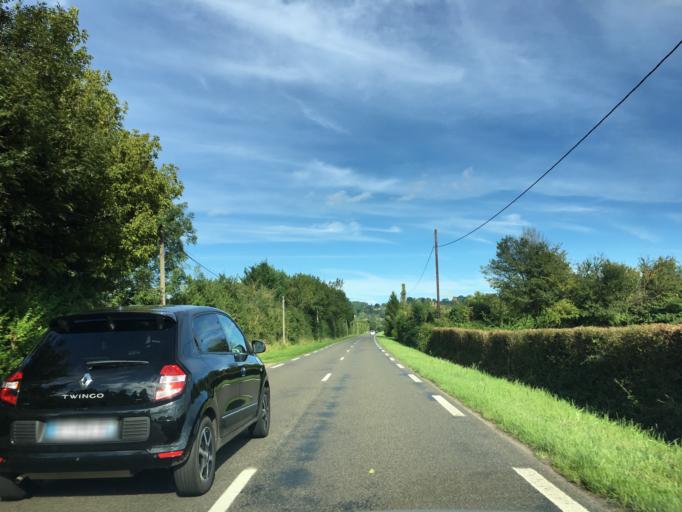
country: FR
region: Lower Normandy
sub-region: Departement du Calvados
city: Cambremer
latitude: 49.1408
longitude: -0.0030
